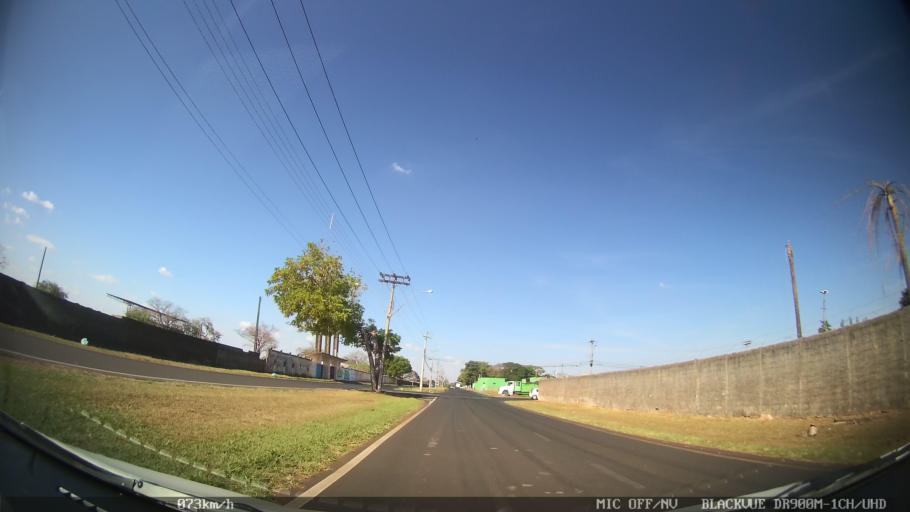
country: BR
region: Sao Paulo
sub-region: Ribeirao Preto
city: Ribeirao Preto
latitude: -21.1502
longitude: -47.7675
